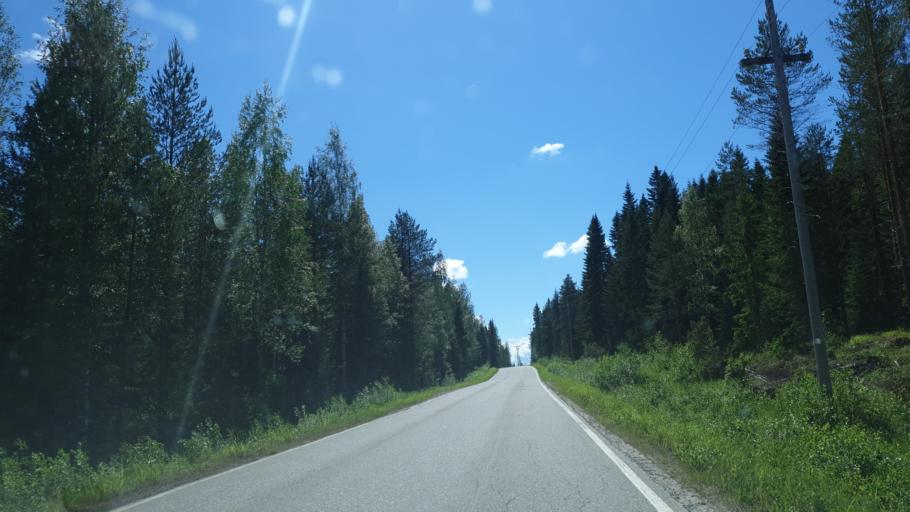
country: FI
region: Northern Savo
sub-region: Koillis-Savo
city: Kaavi
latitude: 63.0351
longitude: 28.5532
